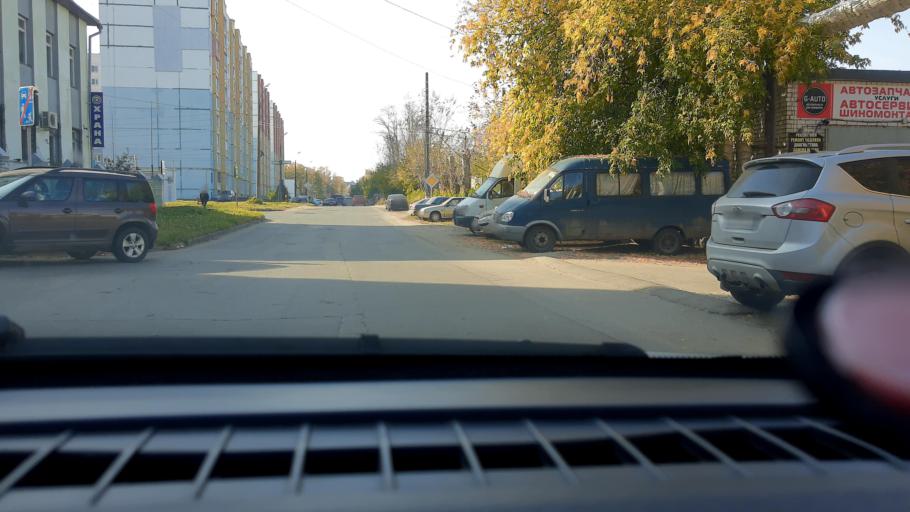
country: RU
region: Nizjnij Novgorod
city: Kstovo
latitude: 56.1563
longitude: 44.2086
